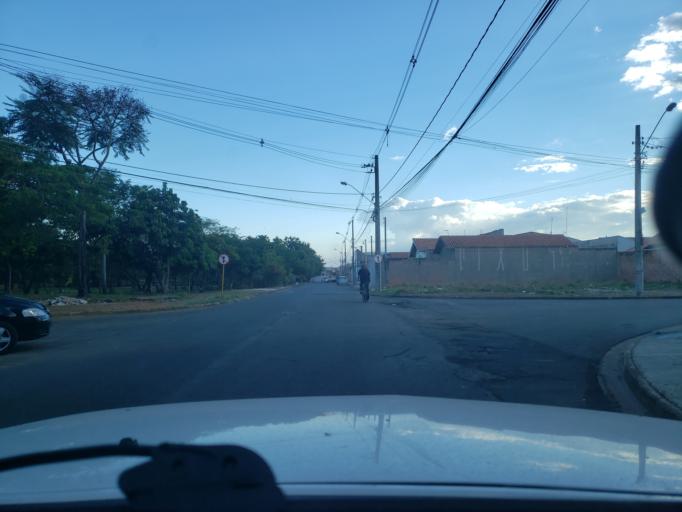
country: BR
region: Sao Paulo
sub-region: Moji-Guacu
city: Mogi-Gaucu
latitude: -22.3291
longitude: -46.9237
